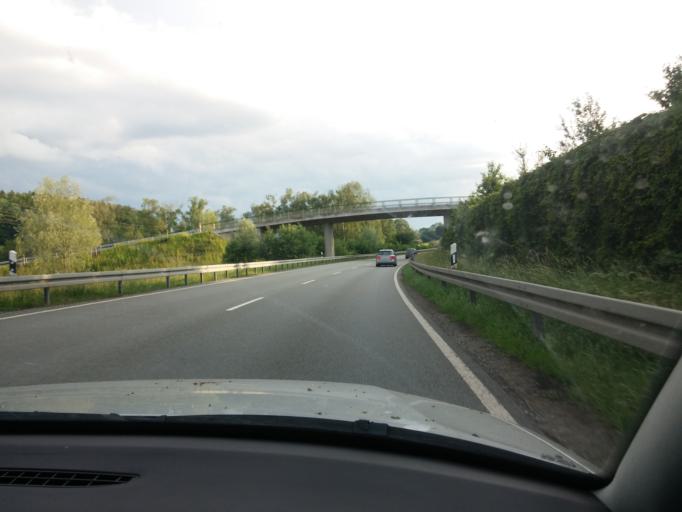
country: DE
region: Bavaria
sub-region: Upper Bavaria
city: Ebersberg
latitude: 48.0741
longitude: 11.9811
